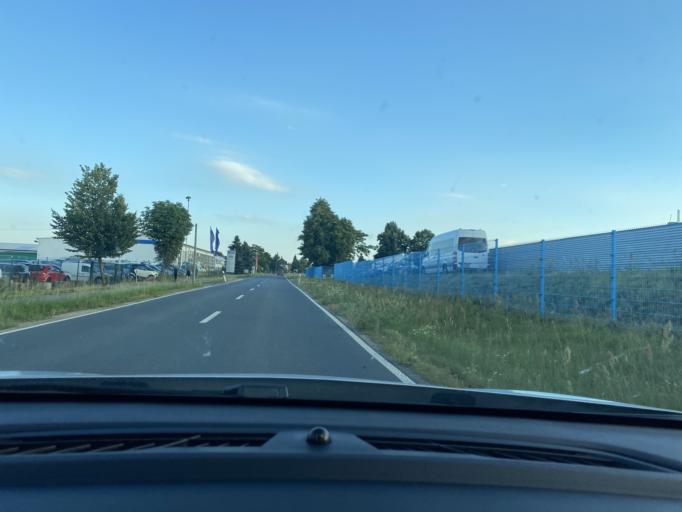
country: DE
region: Saxony
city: Kodersdorf
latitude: 51.2493
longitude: 14.8893
